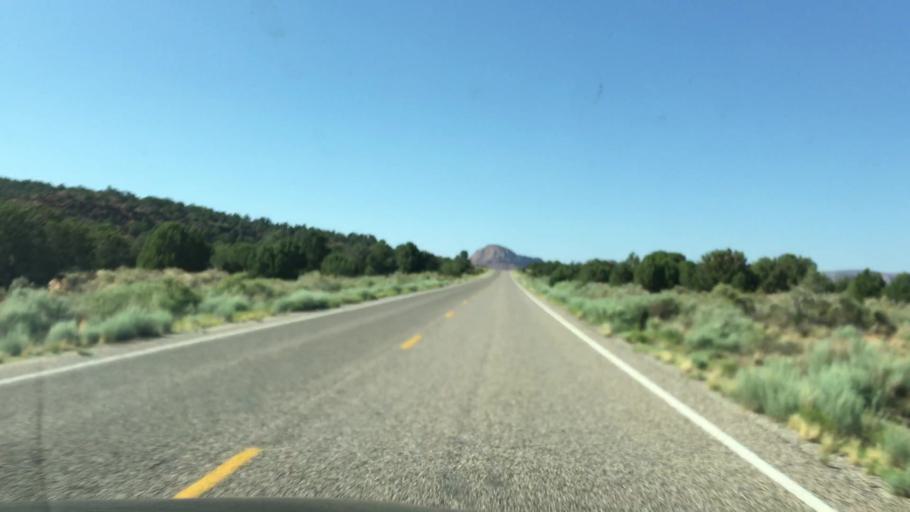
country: US
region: Arizona
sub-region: Coconino County
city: Fredonia
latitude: 36.8680
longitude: -112.7376
